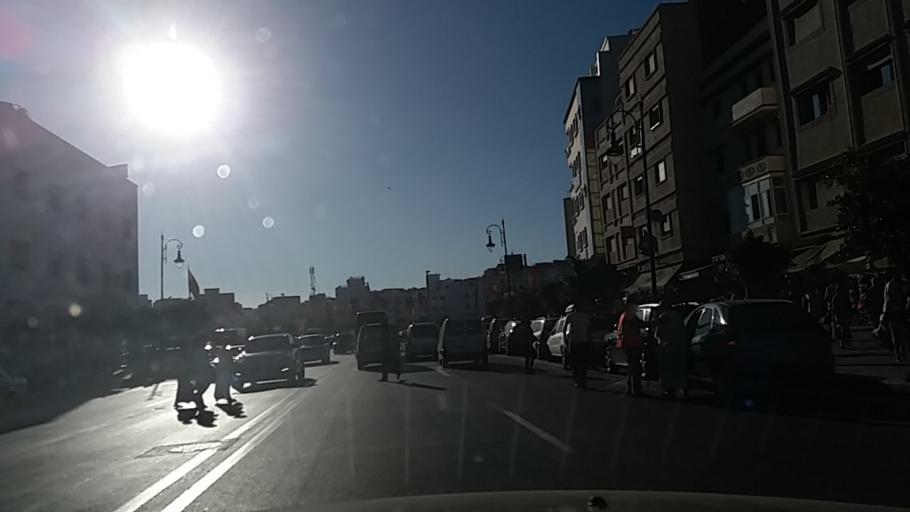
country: MA
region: Tanger-Tetouan
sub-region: Tanger-Assilah
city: Tangier
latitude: 35.7534
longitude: -5.8093
